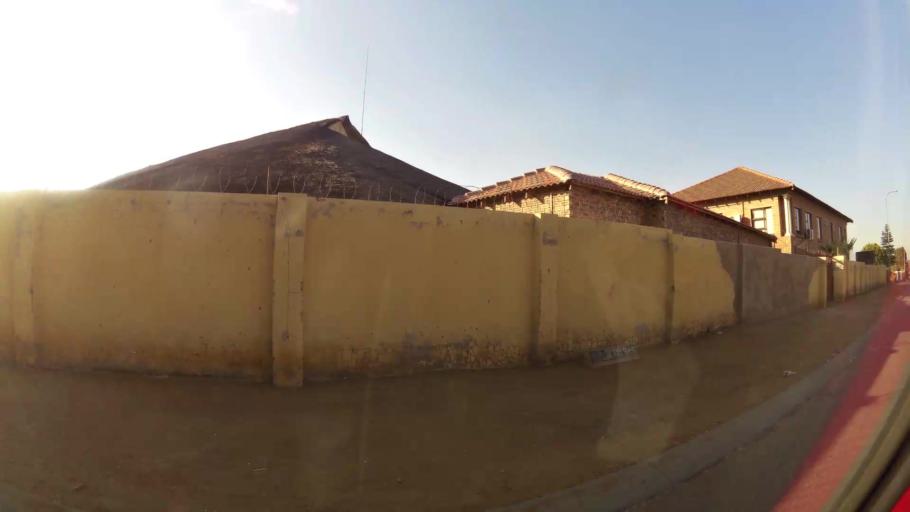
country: ZA
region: North-West
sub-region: Bojanala Platinum District Municipality
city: Rustenburg
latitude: -25.6496
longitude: 27.2193
